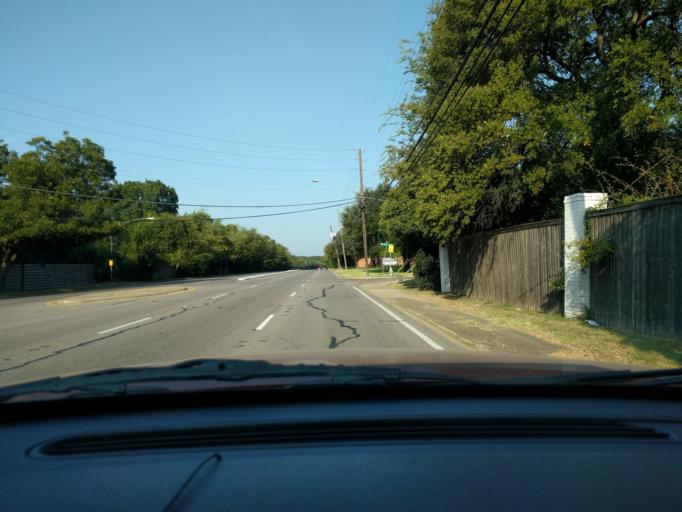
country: US
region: Texas
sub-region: Dallas County
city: University Park
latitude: 32.8657
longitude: -96.8136
